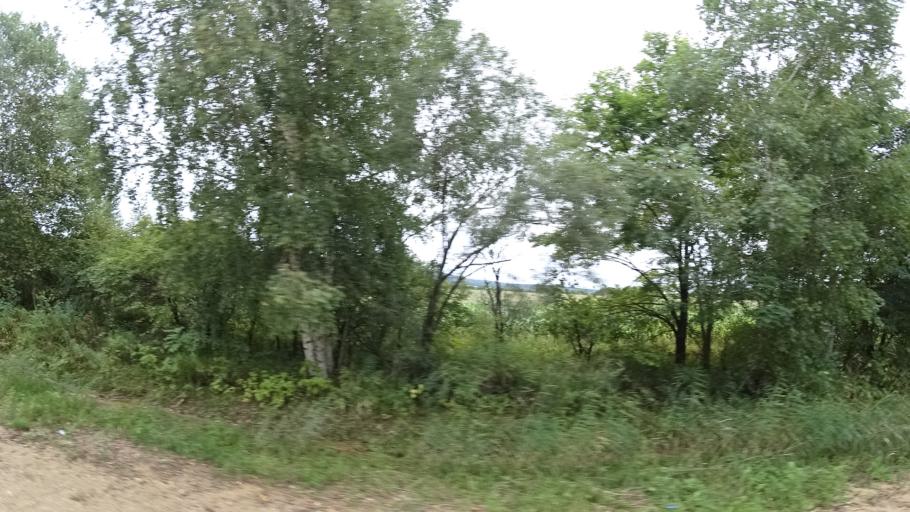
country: RU
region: Primorskiy
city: Rettikhovka
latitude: 44.1597
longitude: 132.6924
